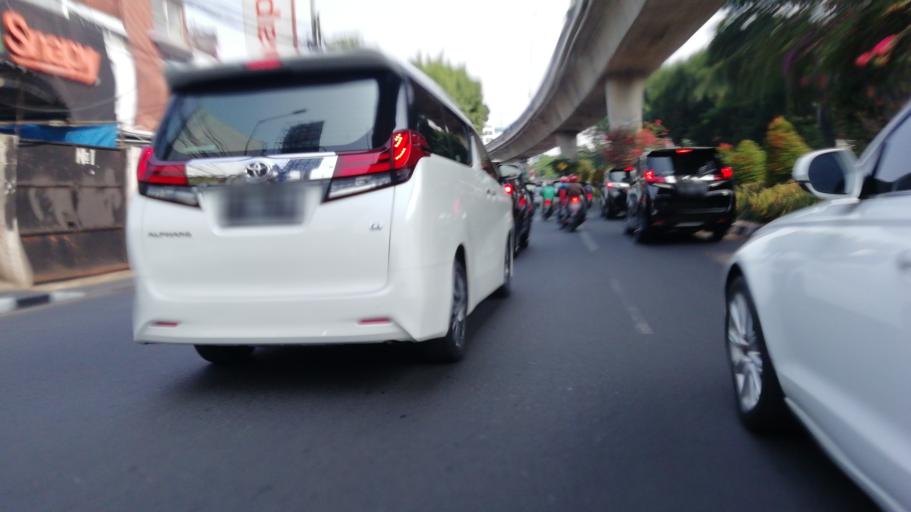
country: ID
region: Jakarta Raya
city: Jakarta
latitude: -6.2480
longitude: 106.8064
